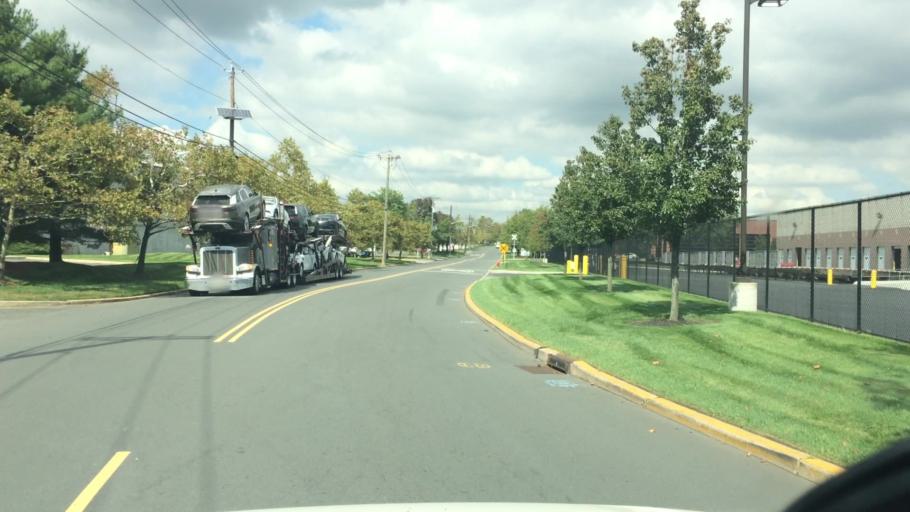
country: US
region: New Jersey
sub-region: Middlesex County
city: Fords
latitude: 40.5158
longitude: -74.3306
